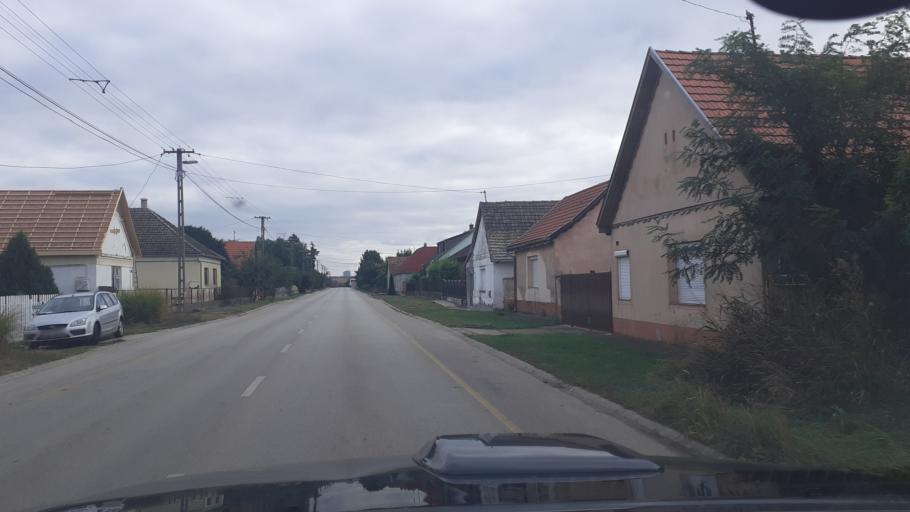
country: HU
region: Fejer
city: Baracs
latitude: 46.9126
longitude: 18.8695
